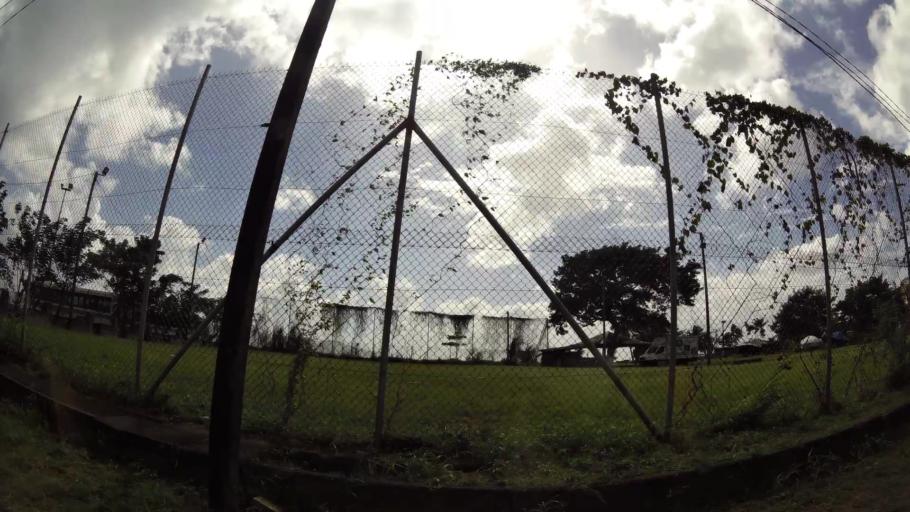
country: MQ
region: Martinique
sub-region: Martinique
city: Fort-de-France
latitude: 14.6016
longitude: -61.0785
